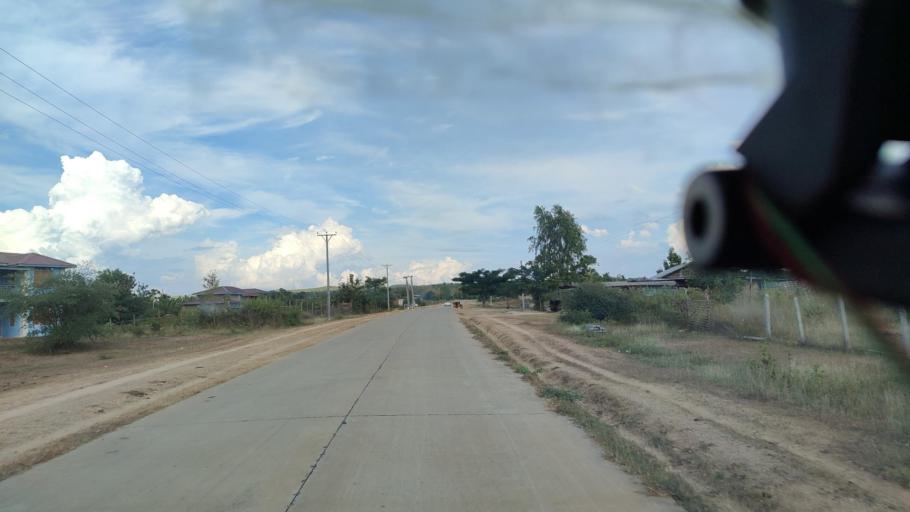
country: MM
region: Mandalay
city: Yamethin
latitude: 20.0950
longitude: 96.0218
